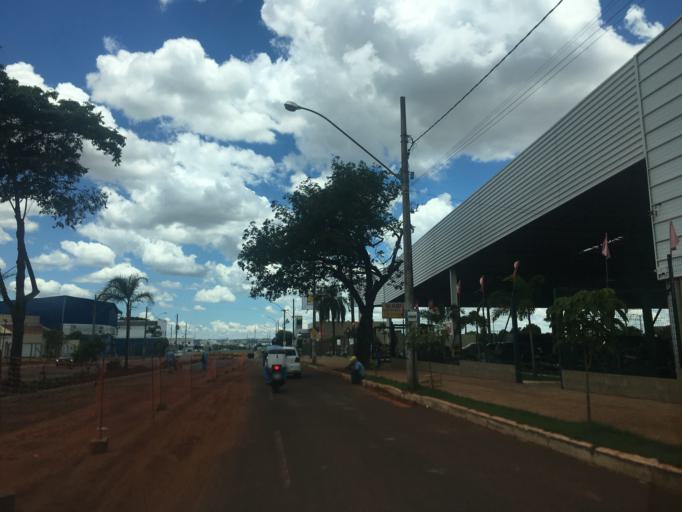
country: BR
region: Minas Gerais
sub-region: Uberlandia
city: Uberlandia
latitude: -18.9412
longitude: -48.3085
